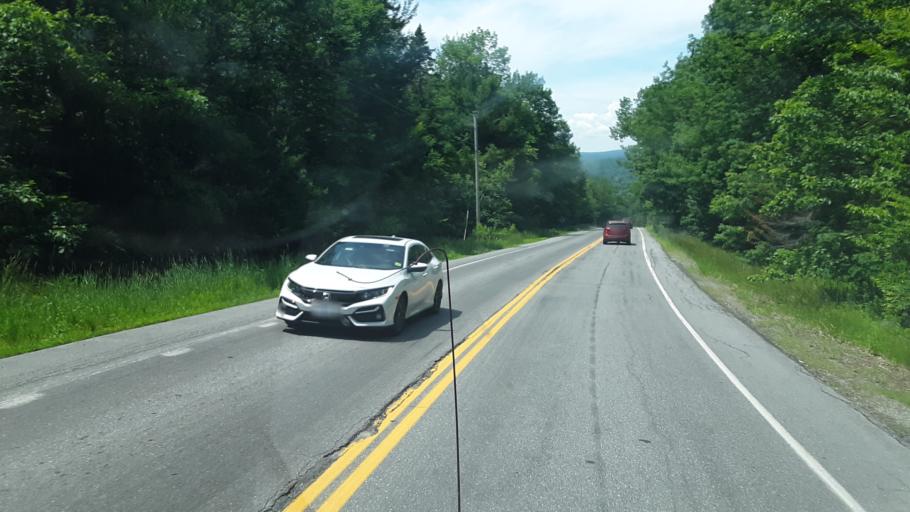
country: US
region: Maine
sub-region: Hancock County
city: Bucksport
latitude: 44.5607
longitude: -68.8426
